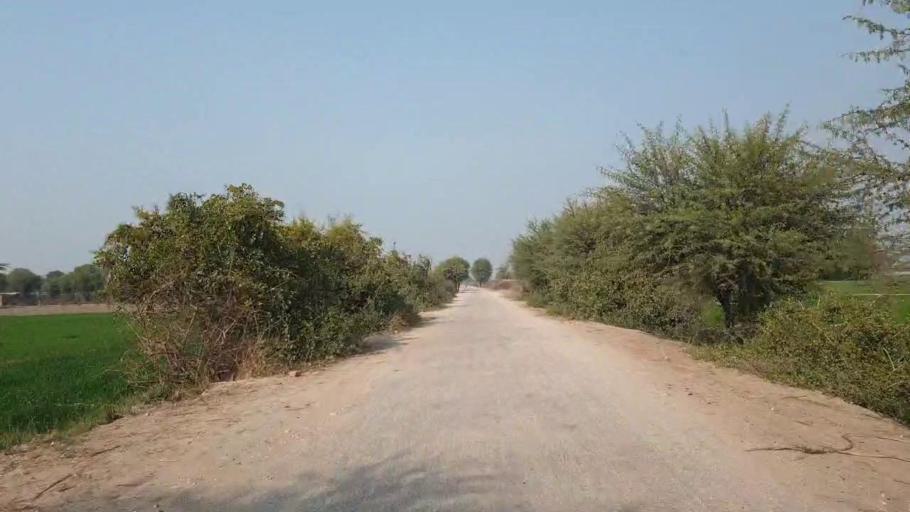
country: PK
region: Sindh
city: Hala
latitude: 25.8499
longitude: 68.4619
